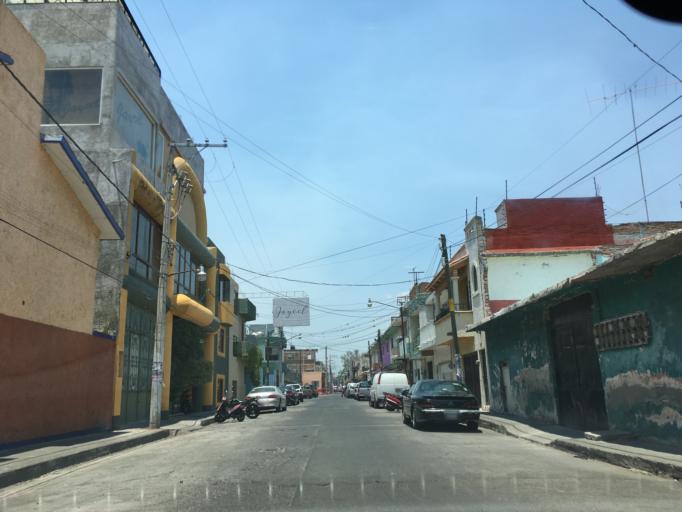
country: MX
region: Guanajuato
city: Moroleon
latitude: 20.1309
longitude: -101.1835
